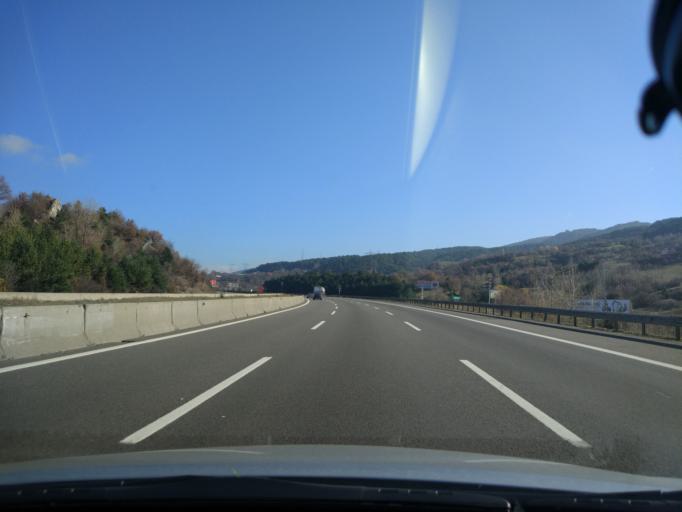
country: TR
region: Bolu
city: Bolu
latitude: 40.7340
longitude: 31.8065
